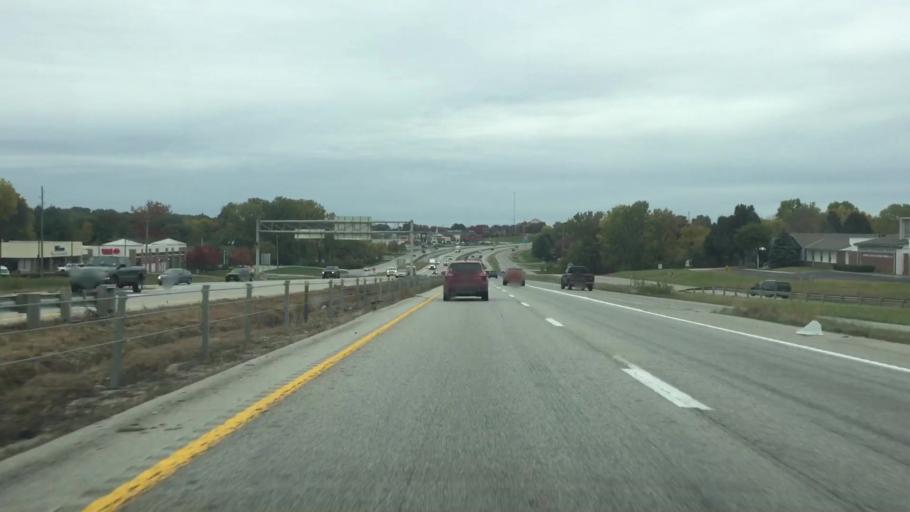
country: US
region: Missouri
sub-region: Jackson County
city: Lees Summit
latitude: 38.9123
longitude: -94.3951
